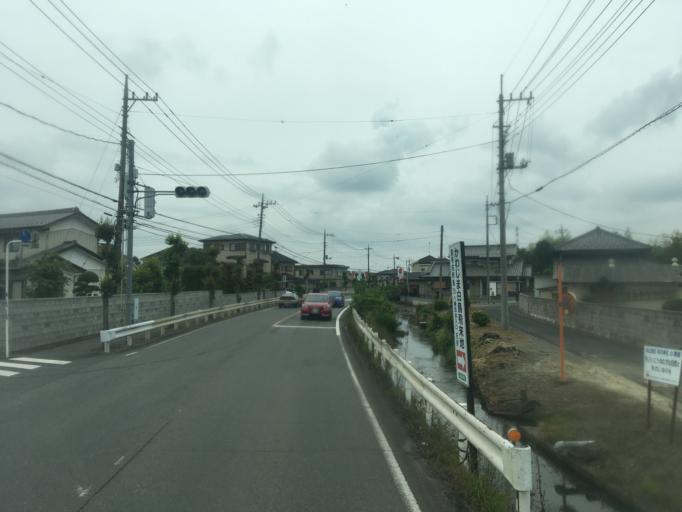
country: JP
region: Saitama
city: Sakado
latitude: 35.9848
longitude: 139.4525
